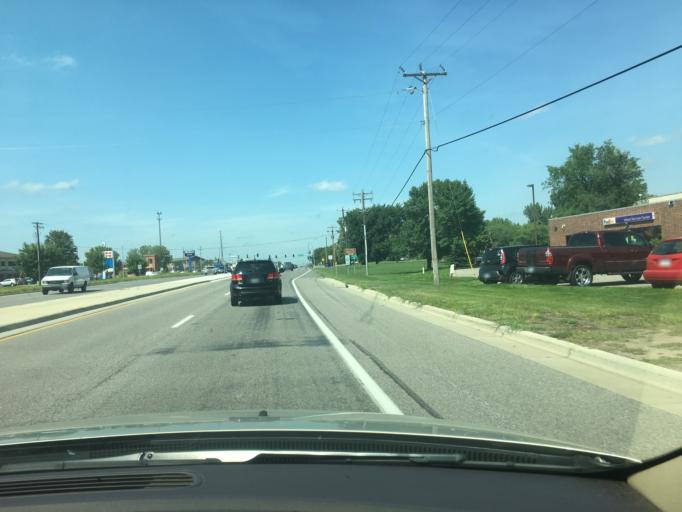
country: US
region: Minnesota
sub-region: Stearns County
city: Saint Augusta
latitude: 45.5127
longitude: -94.1592
